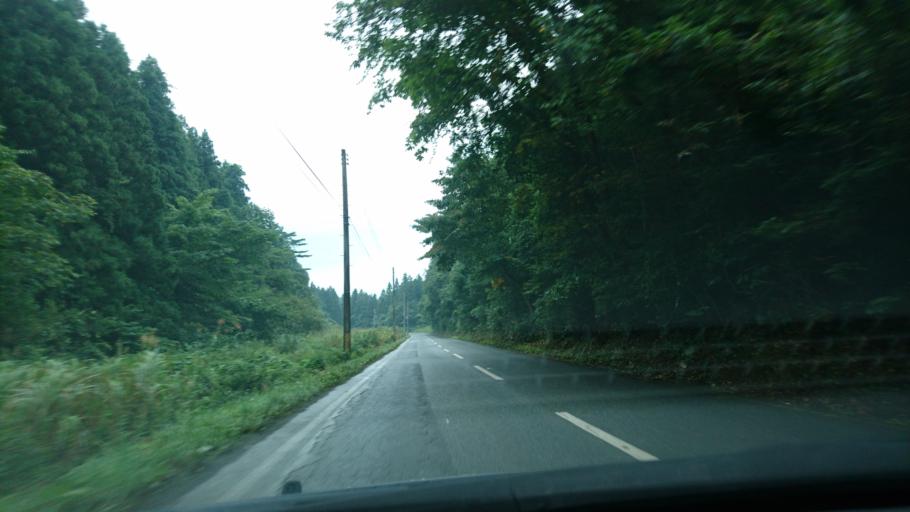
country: JP
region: Iwate
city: Mizusawa
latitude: 39.0329
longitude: 141.1991
